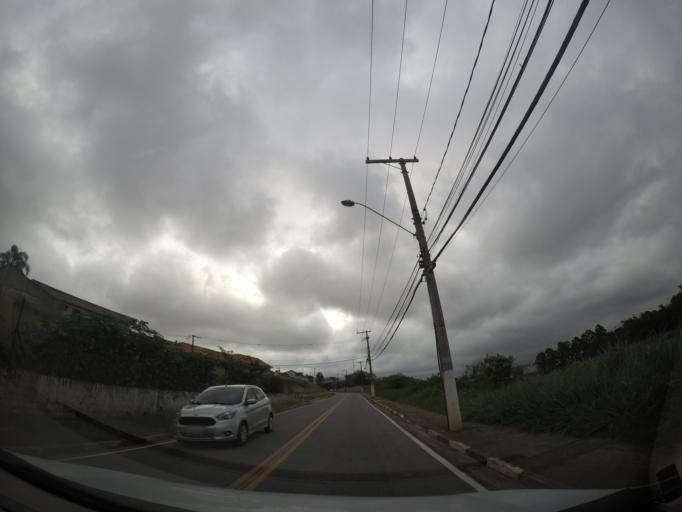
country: BR
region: Sao Paulo
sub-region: Aruja
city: Aruja
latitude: -23.4014
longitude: -46.3441
